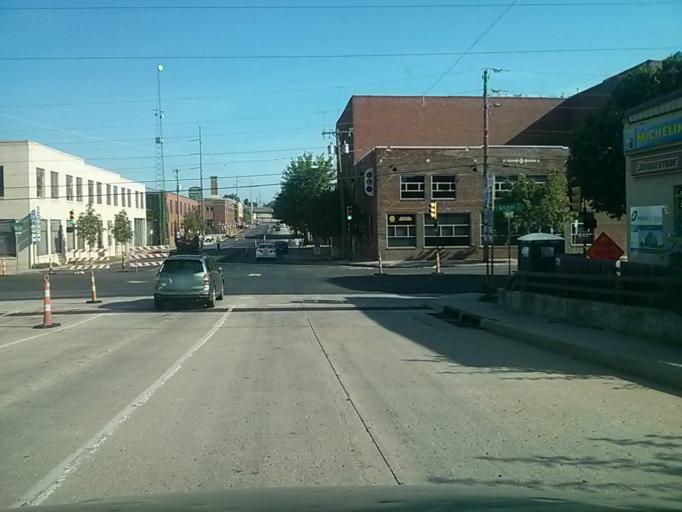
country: US
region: Oklahoma
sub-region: Tulsa County
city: Tulsa
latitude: 36.1583
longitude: -95.9894
